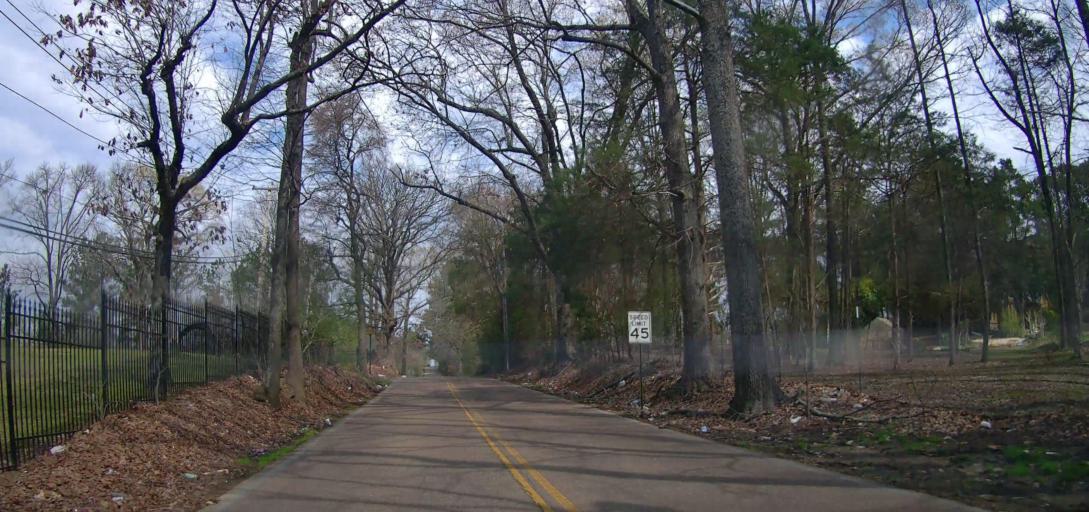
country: US
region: Mississippi
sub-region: De Soto County
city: Olive Branch
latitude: 34.9952
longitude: -89.8484
